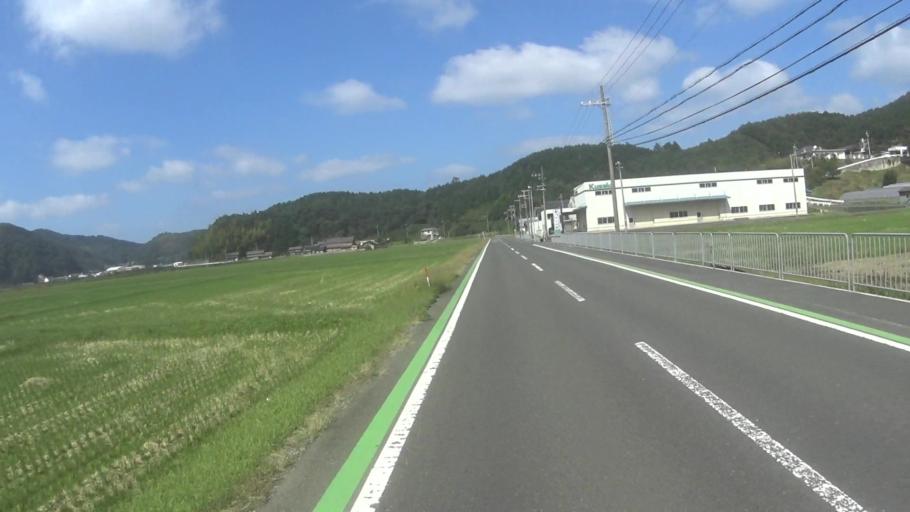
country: JP
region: Kyoto
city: Miyazu
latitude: 35.7231
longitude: 135.1073
